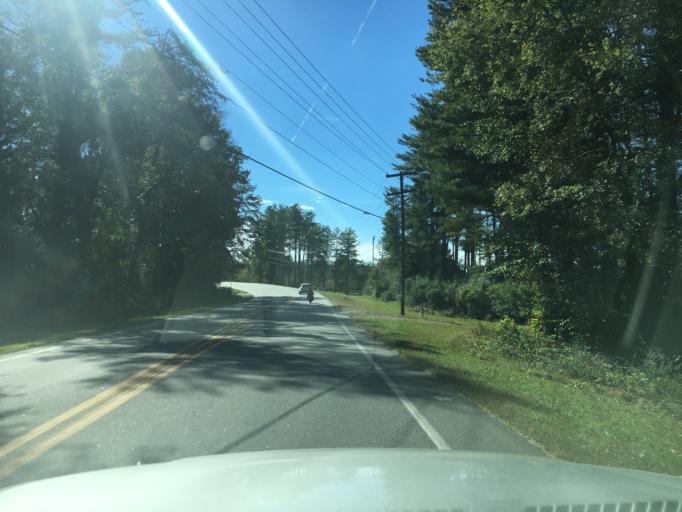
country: US
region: North Carolina
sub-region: Burke County
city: Morganton
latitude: 35.7607
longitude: -81.7008
